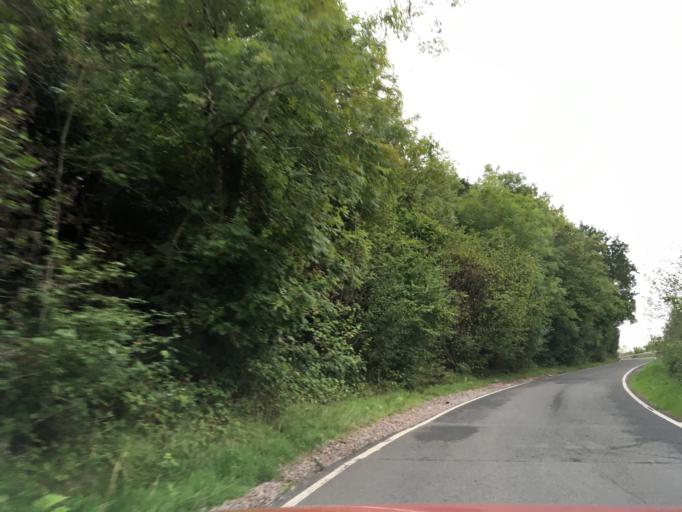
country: GB
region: Wales
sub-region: Newport
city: Langstone
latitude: 51.6230
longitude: -2.9033
